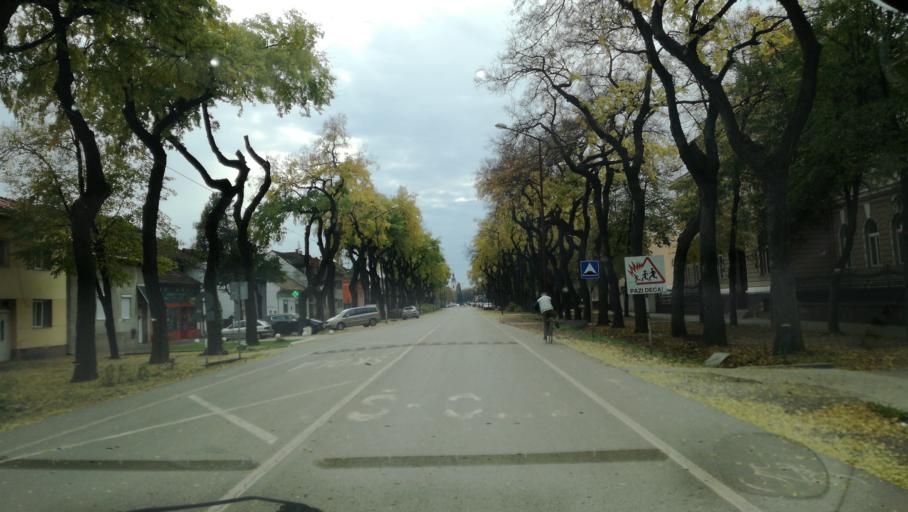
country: RS
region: Autonomna Pokrajina Vojvodina
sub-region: Severnobanatski Okrug
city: Kikinda
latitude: 45.8350
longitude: 20.4737
